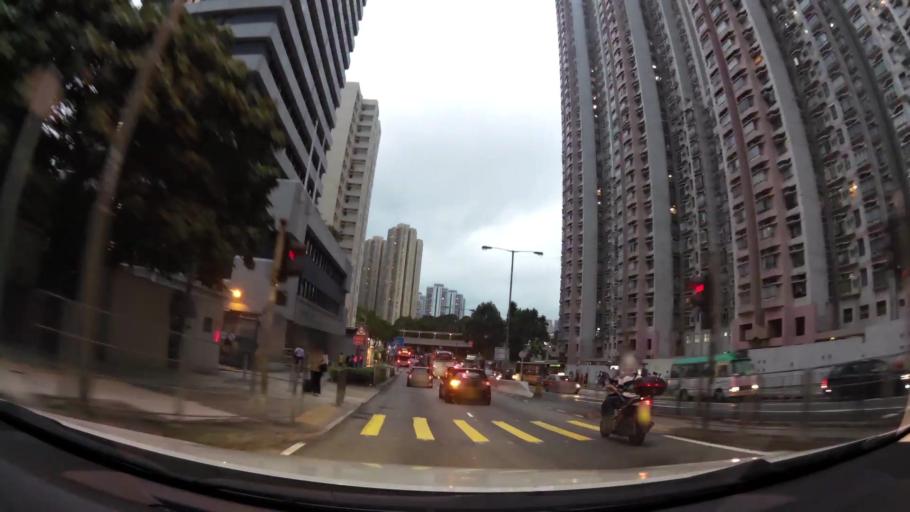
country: HK
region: Tsuen Wan
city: Tsuen Wan
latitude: 22.3512
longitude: 114.1080
